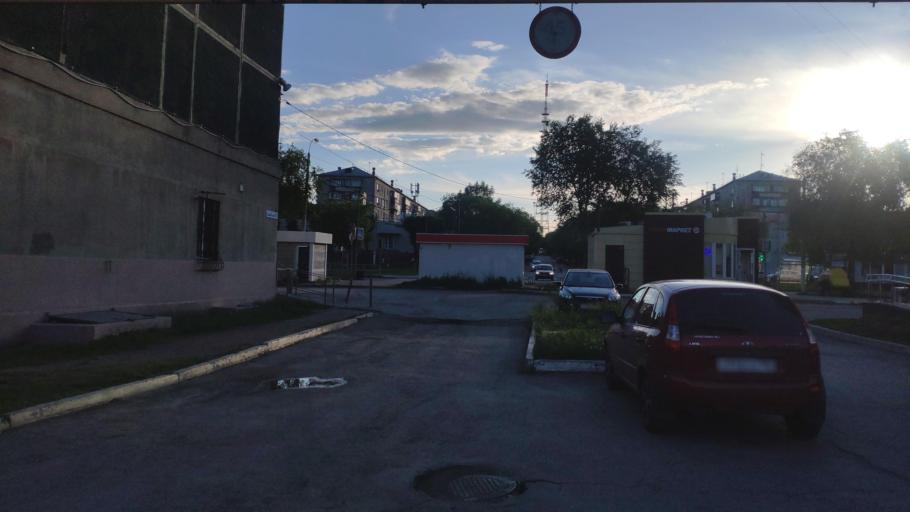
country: RU
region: Chelyabinsk
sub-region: Gorod Magnitogorsk
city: Magnitogorsk
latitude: 53.4080
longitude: 58.9627
